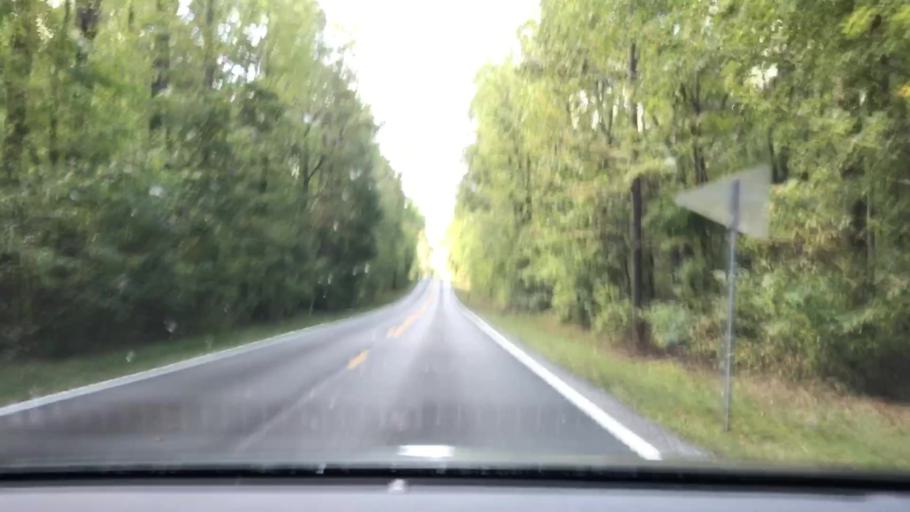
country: US
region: Kentucky
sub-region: Graves County
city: Mayfield
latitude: 36.8730
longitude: -88.5692
